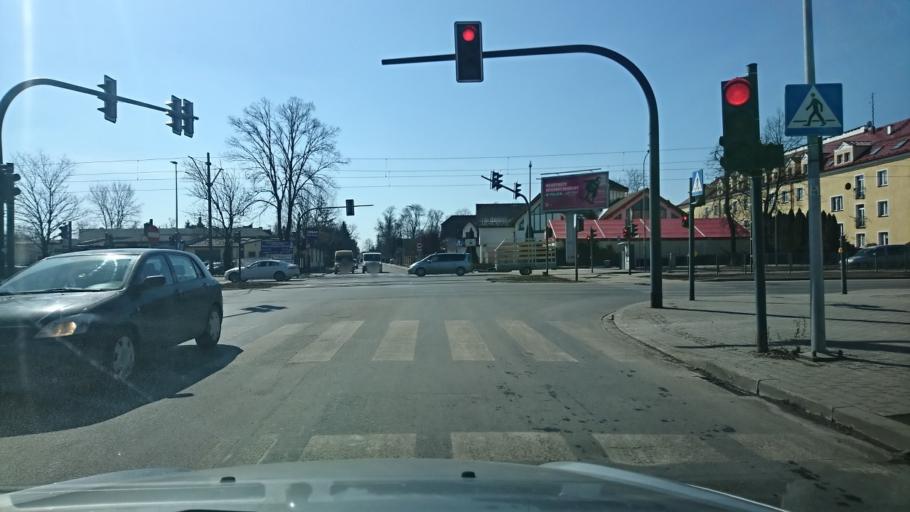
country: PL
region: Lesser Poland Voivodeship
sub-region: Powiat wielicki
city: Kokotow
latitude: 50.0688
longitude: 20.0526
